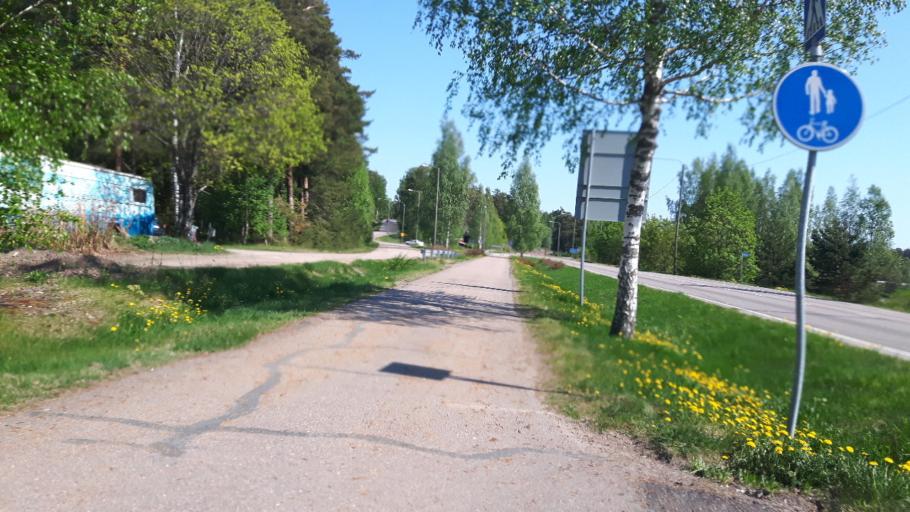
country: FI
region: Kymenlaakso
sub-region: Kotka-Hamina
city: Broby
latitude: 60.4947
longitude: 26.7249
